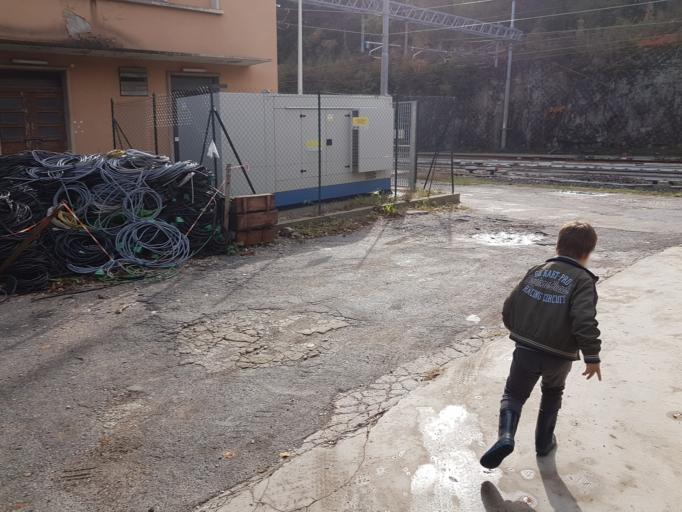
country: IT
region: Friuli Venezia Giulia
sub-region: Provincia di Trieste
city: Aurisina Cave
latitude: 45.7541
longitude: 13.6563
